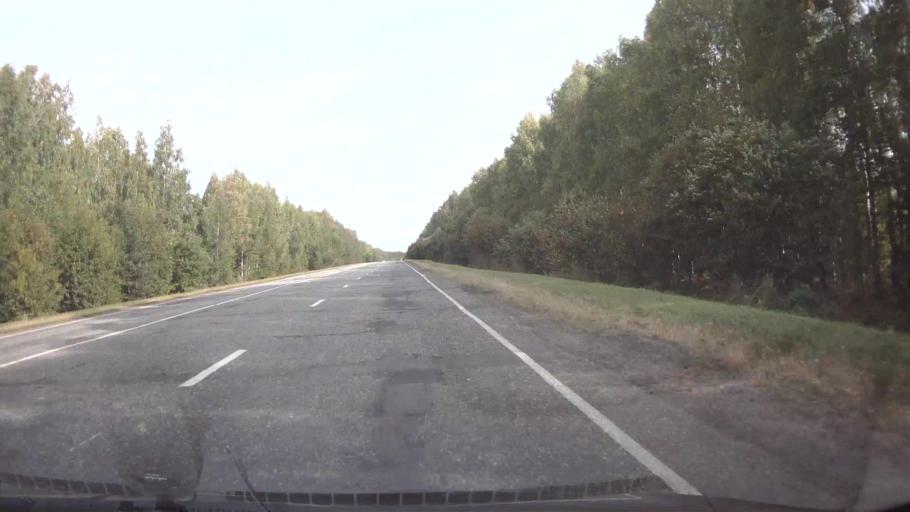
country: RU
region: Mariy-El
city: Sovetskiy
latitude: 56.7999
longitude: 48.6879
